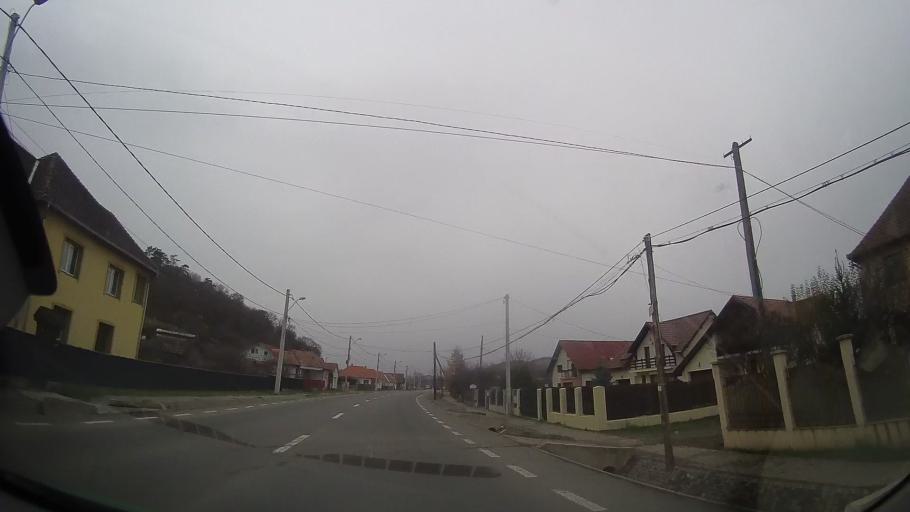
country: RO
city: Remetea
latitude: 46.5968
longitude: 24.5315
